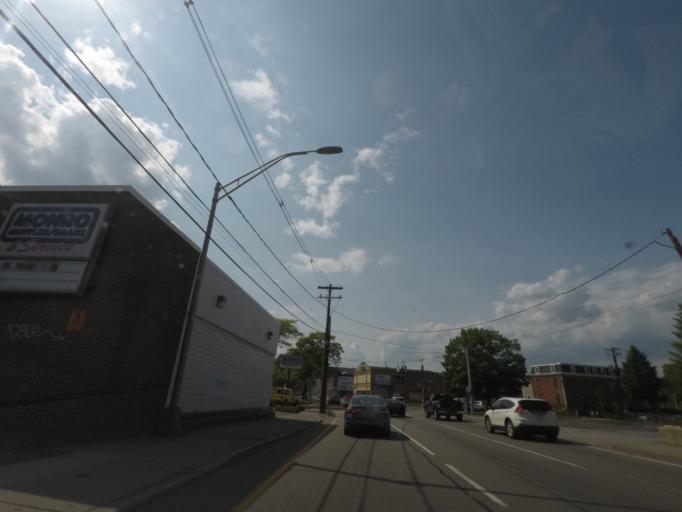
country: US
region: New York
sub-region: Dutchess County
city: Poughkeepsie
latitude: 41.7032
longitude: -73.9223
